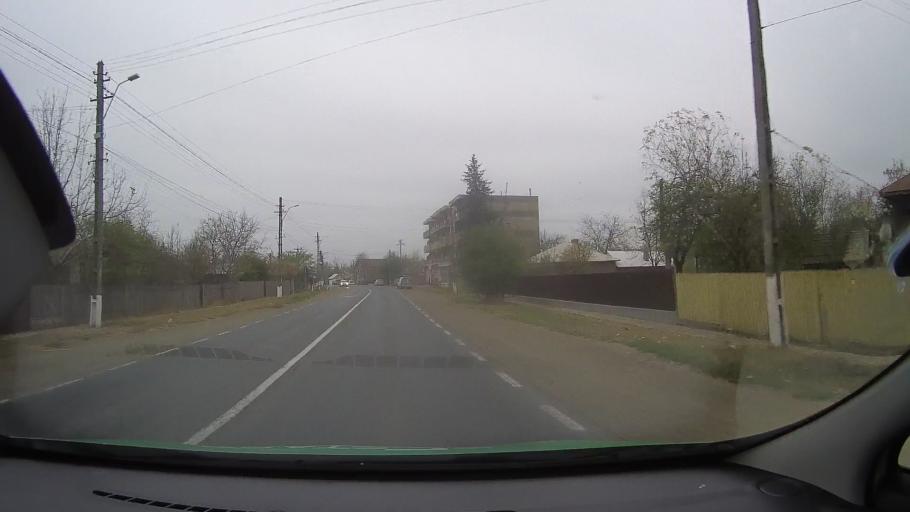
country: RO
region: Braila
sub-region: Comuna Baraganul
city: Baraganul
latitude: 44.8116
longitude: 27.5142
